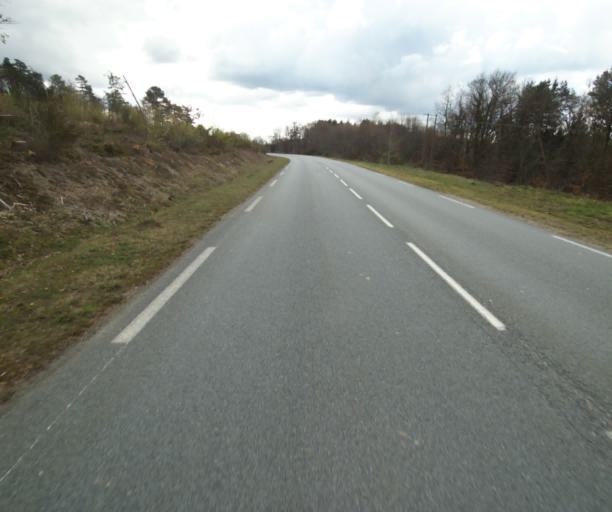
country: FR
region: Limousin
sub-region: Departement de la Correze
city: Correze
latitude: 45.2867
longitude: 1.9046
